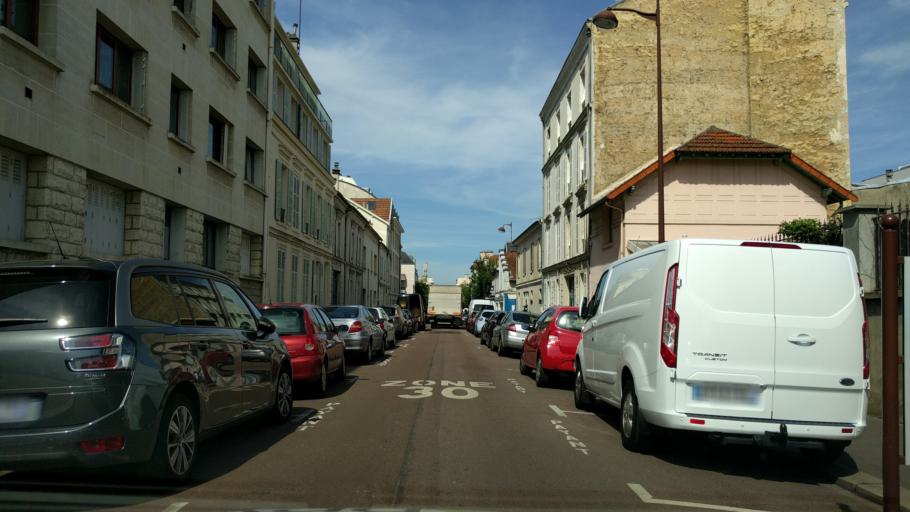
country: FR
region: Ile-de-France
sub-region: Departement des Yvelines
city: Versailles
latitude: 48.8102
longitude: 2.1402
